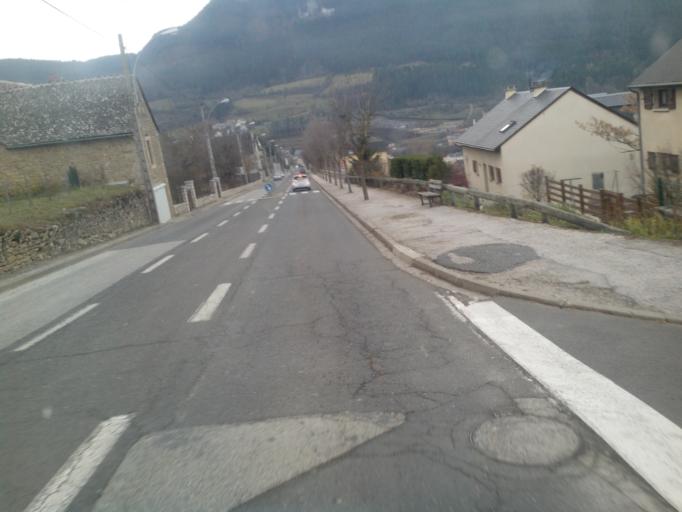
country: FR
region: Languedoc-Roussillon
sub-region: Departement de la Lozere
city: Mende
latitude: 44.5234
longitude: 3.4832
